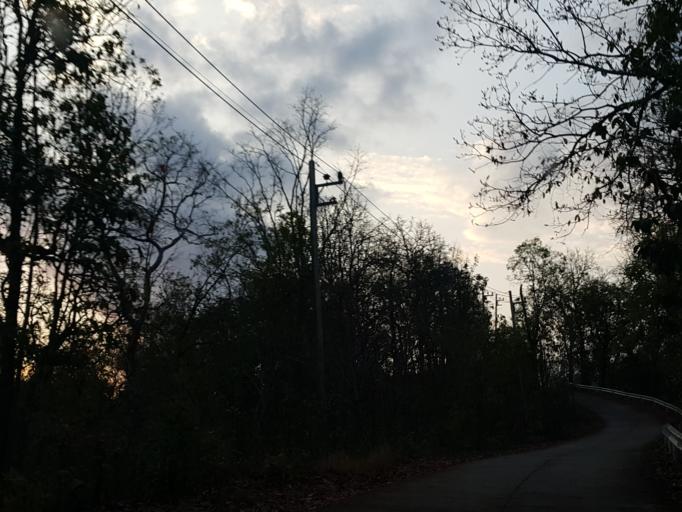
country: TH
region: Lampang
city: Mueang Pan
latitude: 18.8170
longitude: 99.4721
